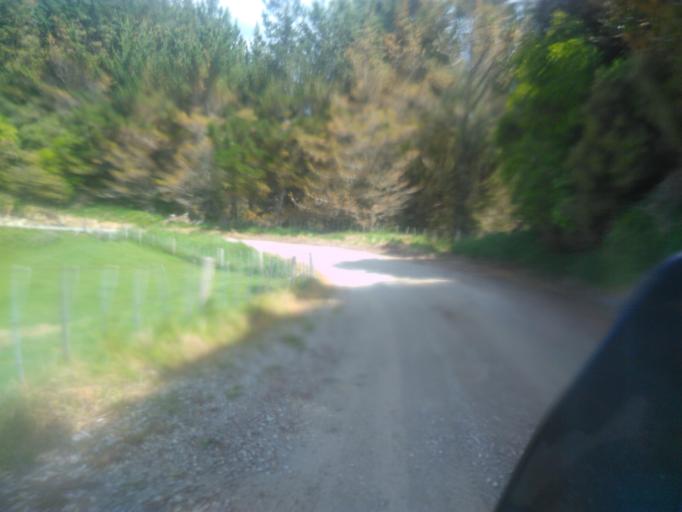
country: NZ
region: Hawke's Bay
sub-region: Wairoa District
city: Wairoa
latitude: -38.7762
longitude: 177.6088
